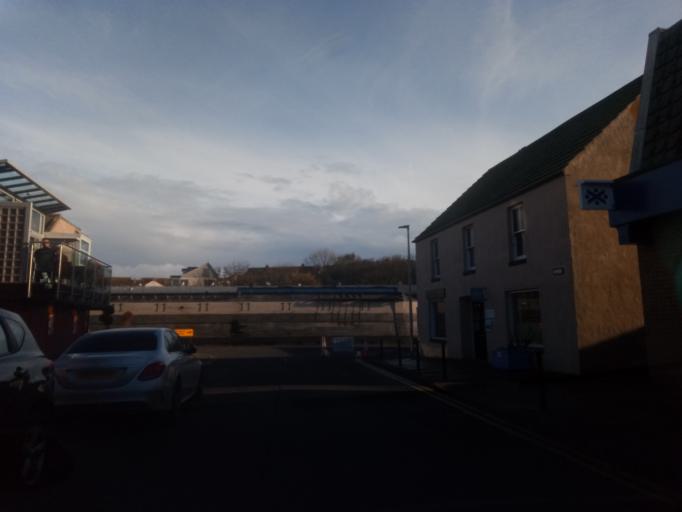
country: GB
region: Scotland
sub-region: The Scottish Borders
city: Eyemouth
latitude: 55.8716
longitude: -2.0887
